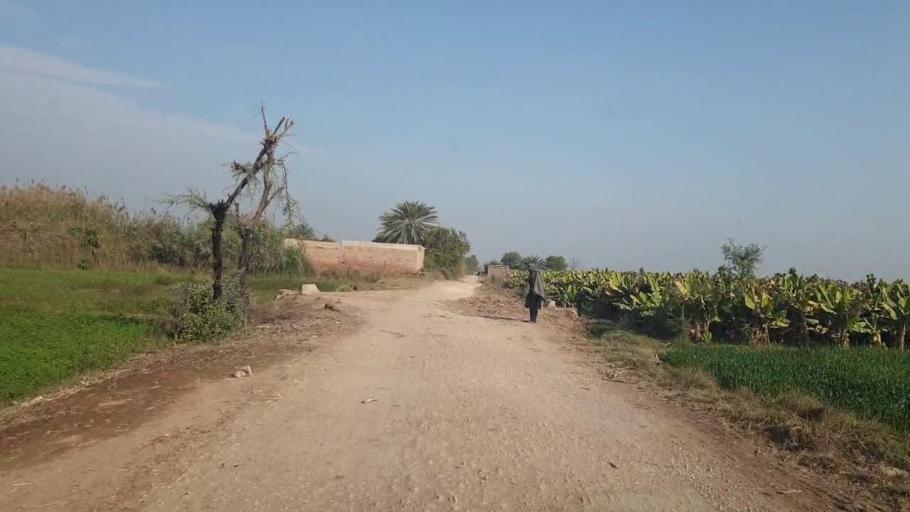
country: PK
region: Sindh
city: Tando Adam
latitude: 25.7470
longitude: 68.6070
